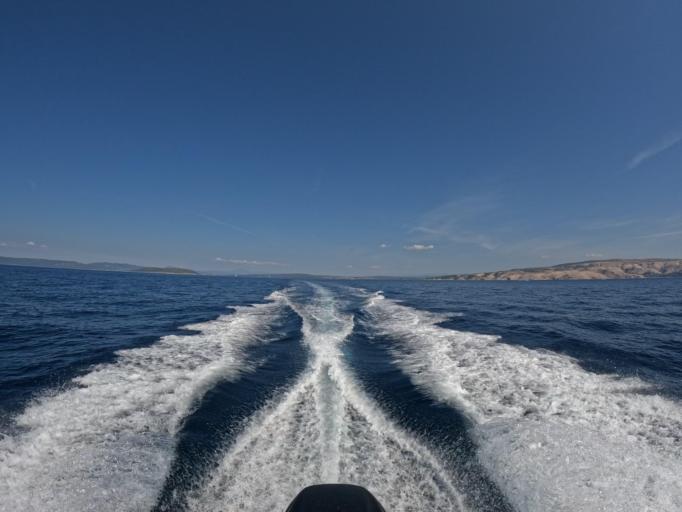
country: HR
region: Primorsko-Goranska
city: Punat
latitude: 44.9181
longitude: 14.6237
